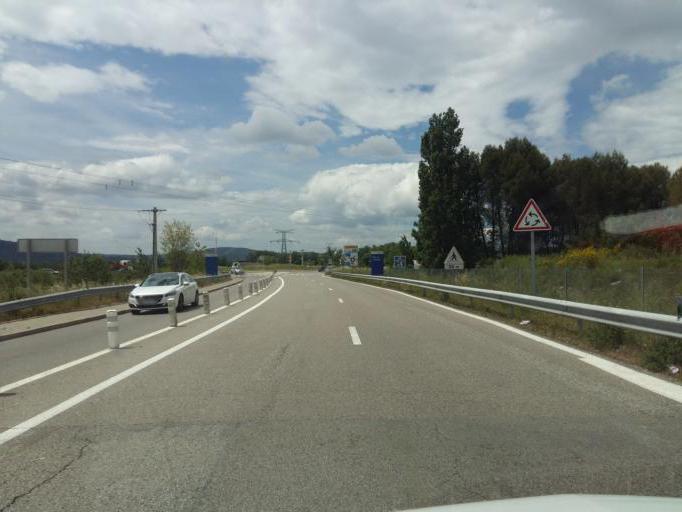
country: FR
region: Provence-Alpes-Cote d'Azur
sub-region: Departement du Vaucluse
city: Pertuis
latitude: 43.6628
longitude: 5.4966
